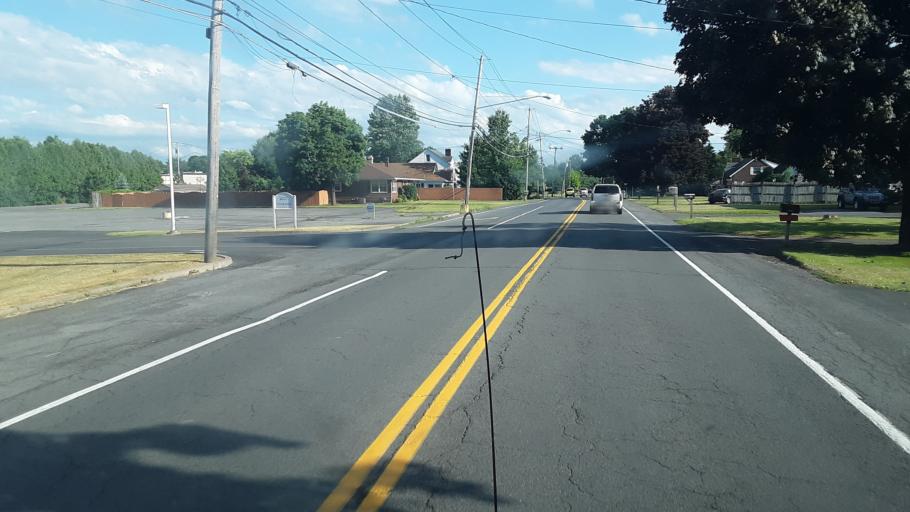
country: US
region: New York
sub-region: Oneida County
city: Rome
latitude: 43.2402
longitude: -75.4555
